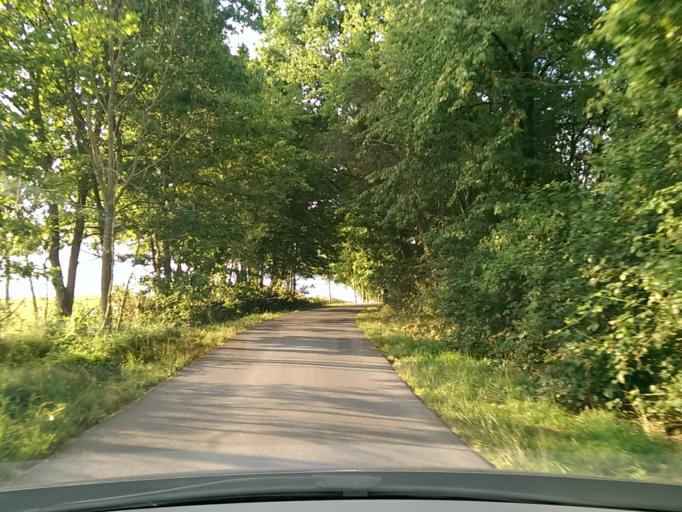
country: CZ
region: Central Bohemia
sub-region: Okres Mlada Boleslav
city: Zd'ar
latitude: 50.5385
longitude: 15.1220
